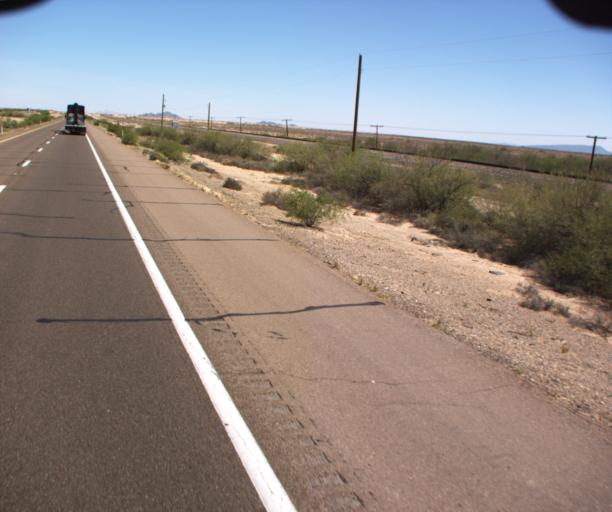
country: US
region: Arizona
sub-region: Yuma County
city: Wellton
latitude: 32.7534
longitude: -113.6539
